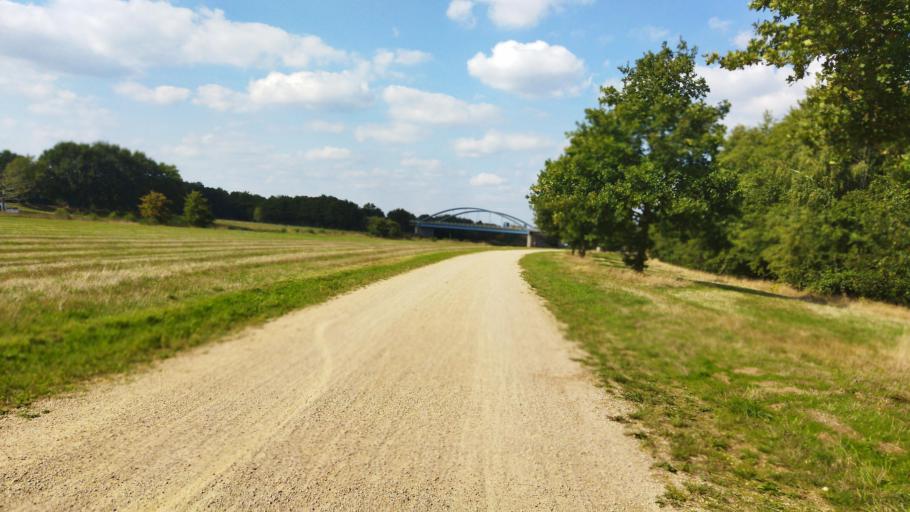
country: DE
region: Lower Saxony
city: Haren
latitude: 52.7833
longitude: 7.2549
